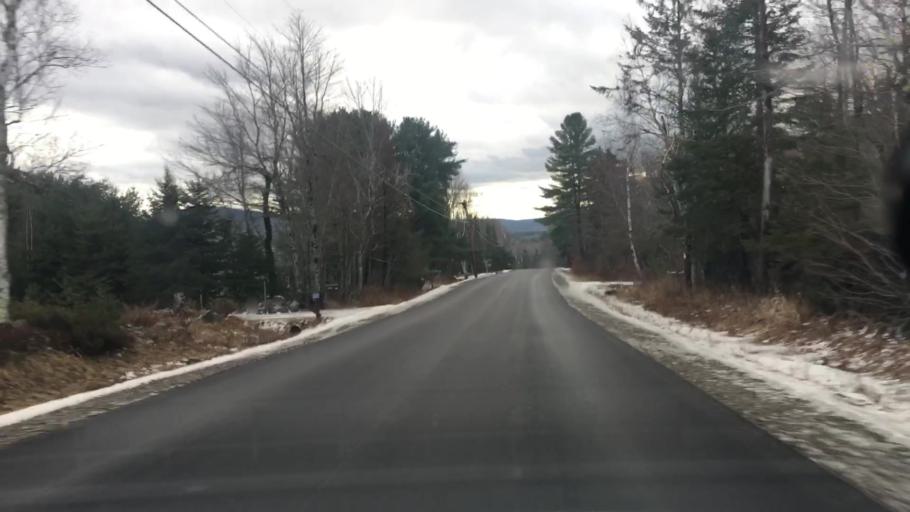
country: US
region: Maine
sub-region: Hancock County
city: Dedham
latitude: 44.6564
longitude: -68.7042
